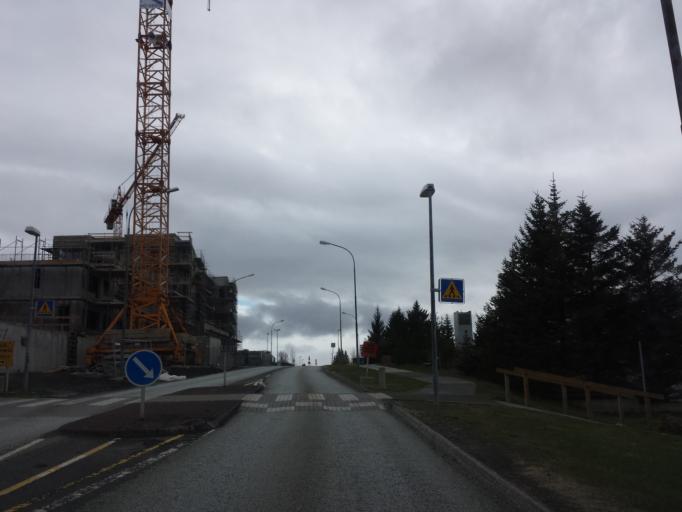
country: IS
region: Capital Region
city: Gardabaer
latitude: 64.0899
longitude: -21.9210
